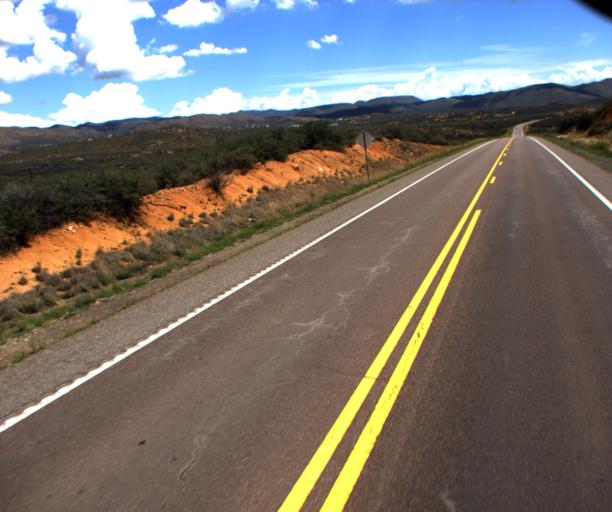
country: US
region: Arizona
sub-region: Yavapai County
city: Dewey-Humboldt
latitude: 34.5447
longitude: -112.1822
